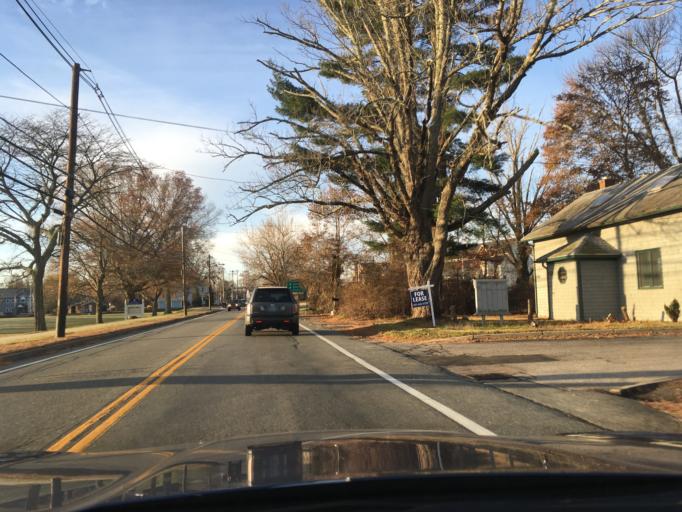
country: US
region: Rhode Island
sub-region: Washington County
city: North Kingstown
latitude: 41.5683
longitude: -71.4622
